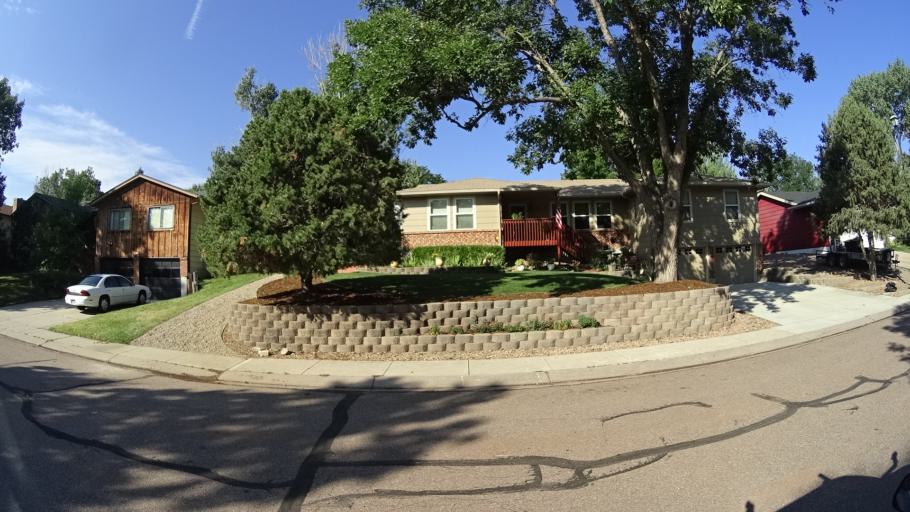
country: US
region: Colorado
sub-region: El Paso County
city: Colorado Springs
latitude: 38.8859
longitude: -104.8424
